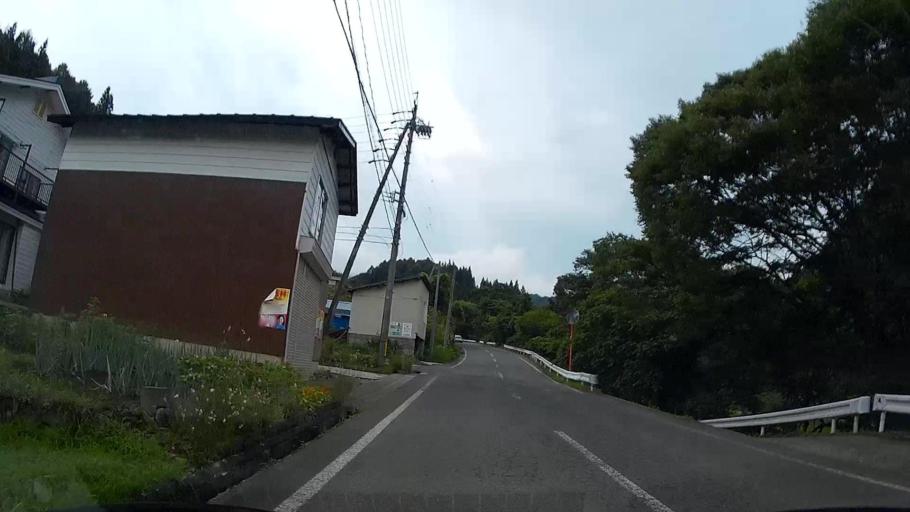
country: JP
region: Nagano
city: Iiyama
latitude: 36.8235
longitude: 138.4315
